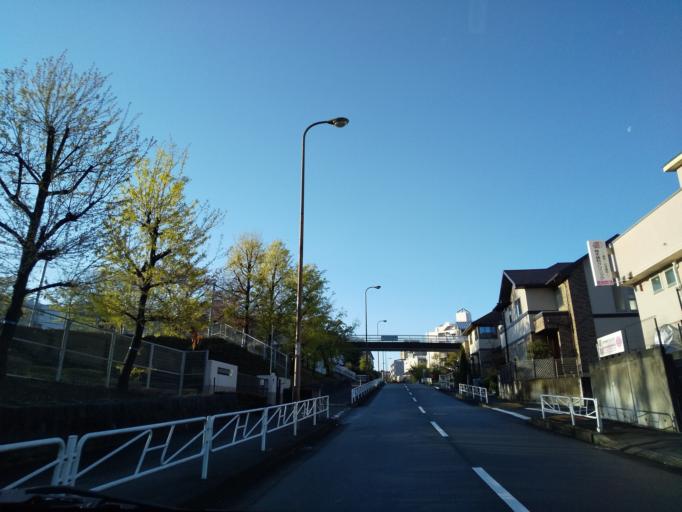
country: JP
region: Tokyo
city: Hachioji
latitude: 35.6159
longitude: 139.3678
